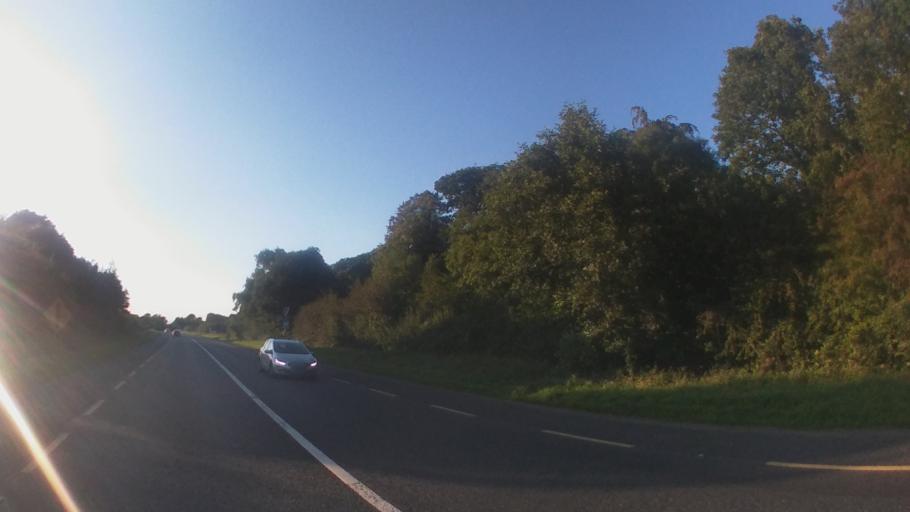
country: IE
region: Leinster
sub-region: Lu
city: Blackrock
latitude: 54.0252
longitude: -6.3433
